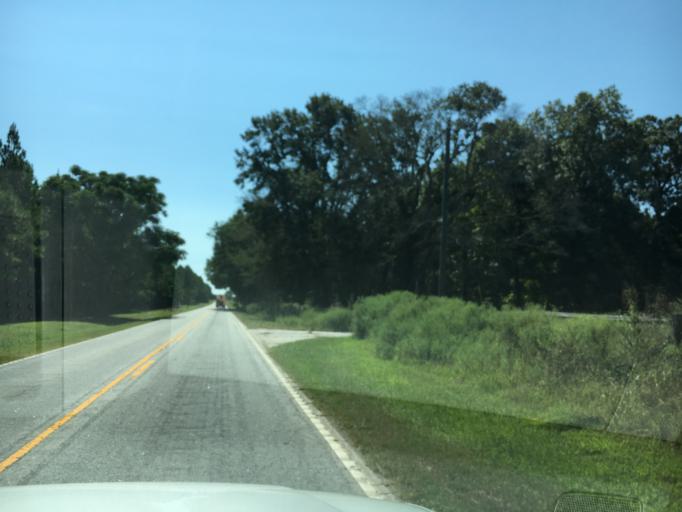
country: US
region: South Carolina
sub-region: Laurens County
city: Joanna
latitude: 34.4092
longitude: -81.8611
